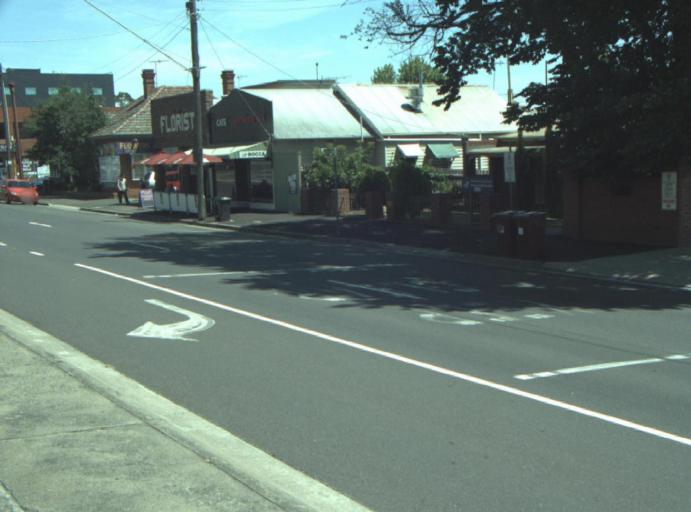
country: AU
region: Victoria
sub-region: Greater Geelong
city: Geelong
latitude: -38.1511
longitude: 144.3658
